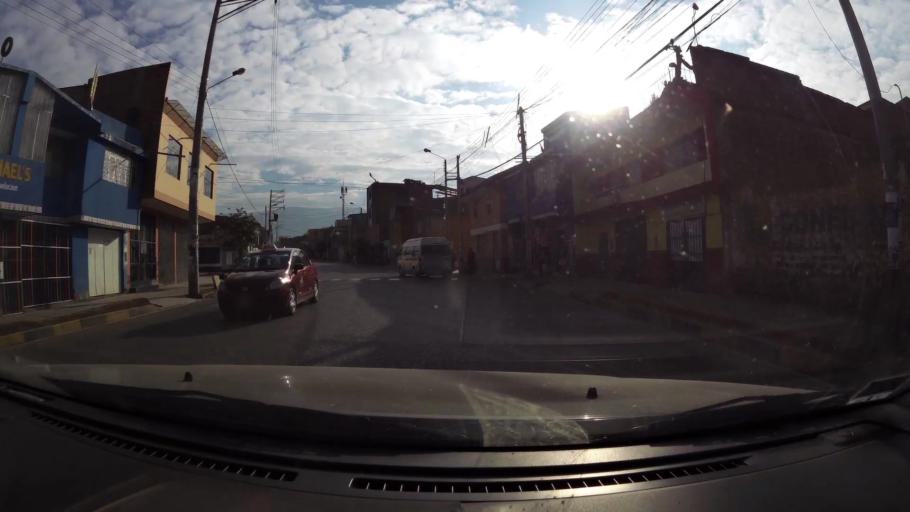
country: PE
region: Junin
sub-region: Provincia de Huancayo
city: Huancayo
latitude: -12.0548
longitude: -75.2033
